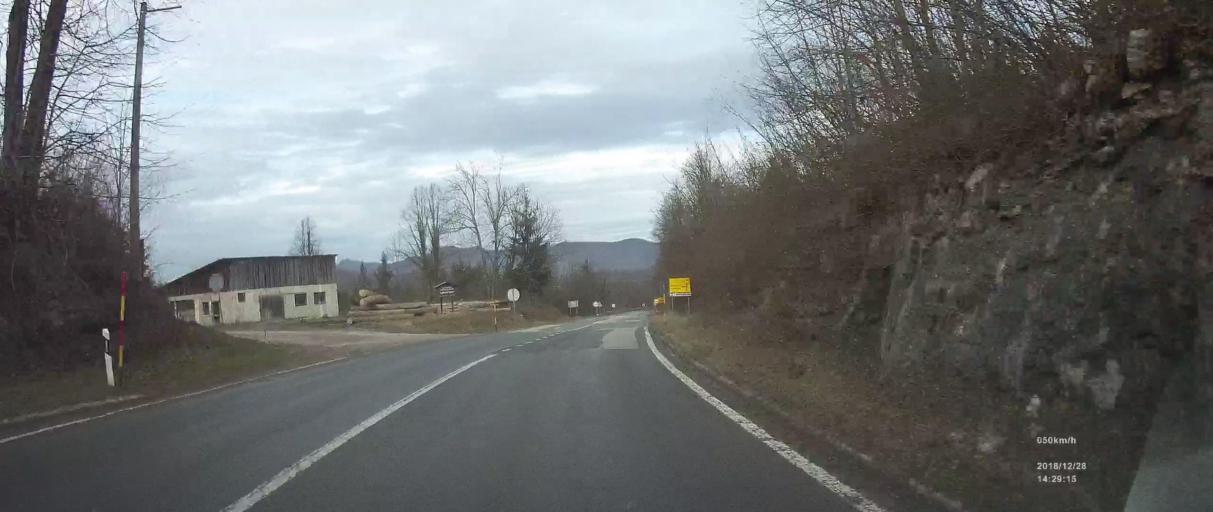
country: HR
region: Primorsko-Goranska
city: Vrbovsko
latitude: 45.4184
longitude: 15.1157
